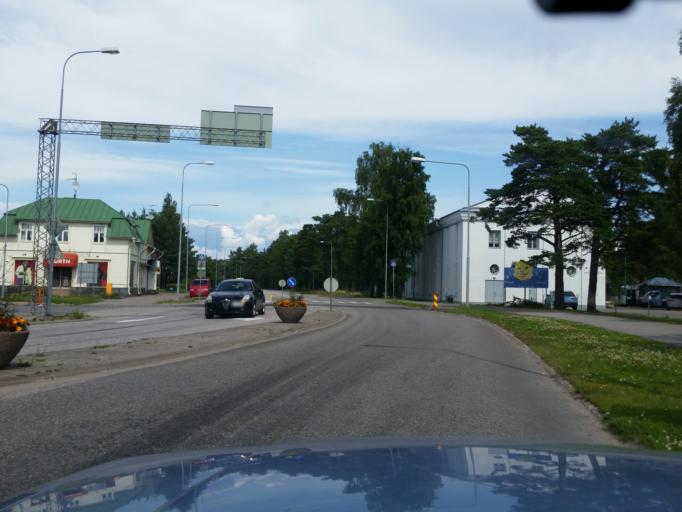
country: FI
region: Uusimaa
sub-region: Raaseporin
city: Hanko
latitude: 59.8316
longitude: 22.9901
